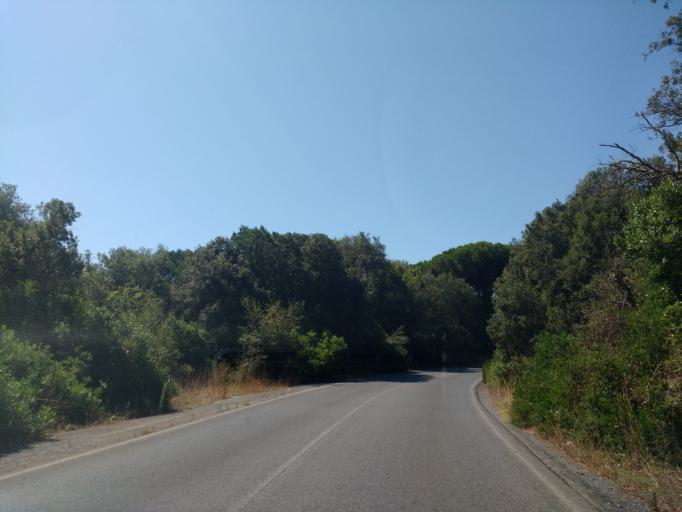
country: IT
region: Latium
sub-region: Citta metropolitana di Roma Capitale
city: Acilia-Castel Fusano-Ostia Antica
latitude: 41.7101
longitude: 12.3576
